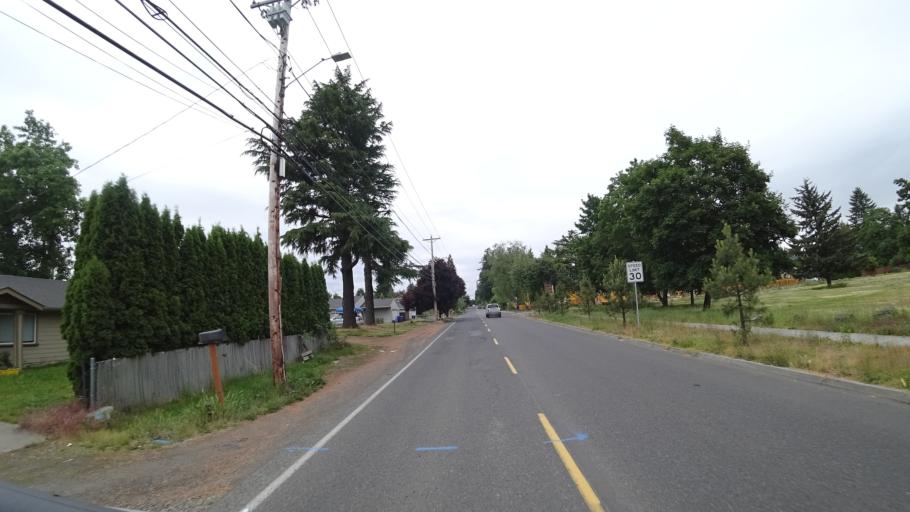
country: US
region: Oregon
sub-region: Clackamas County
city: Happy Valley
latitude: 45.4899
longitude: -122.5236
